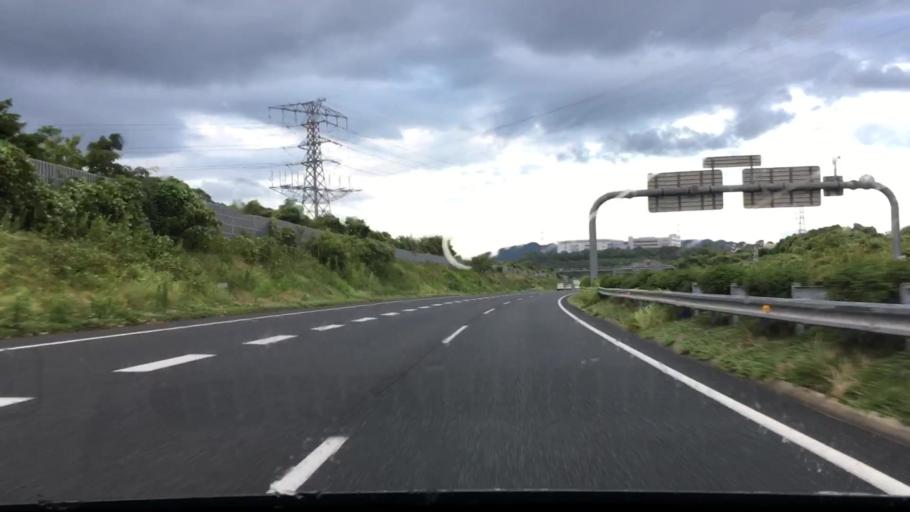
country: JP
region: Fukuoka
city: Kitakyushu
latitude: 33.8237
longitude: 130.8906
